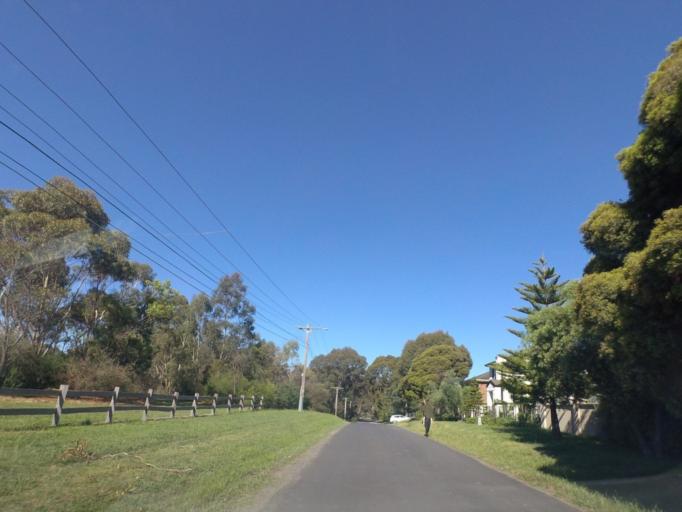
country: AU
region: Victoria
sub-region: Banyule
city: Darch
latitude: -37.7550
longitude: 145.1158
